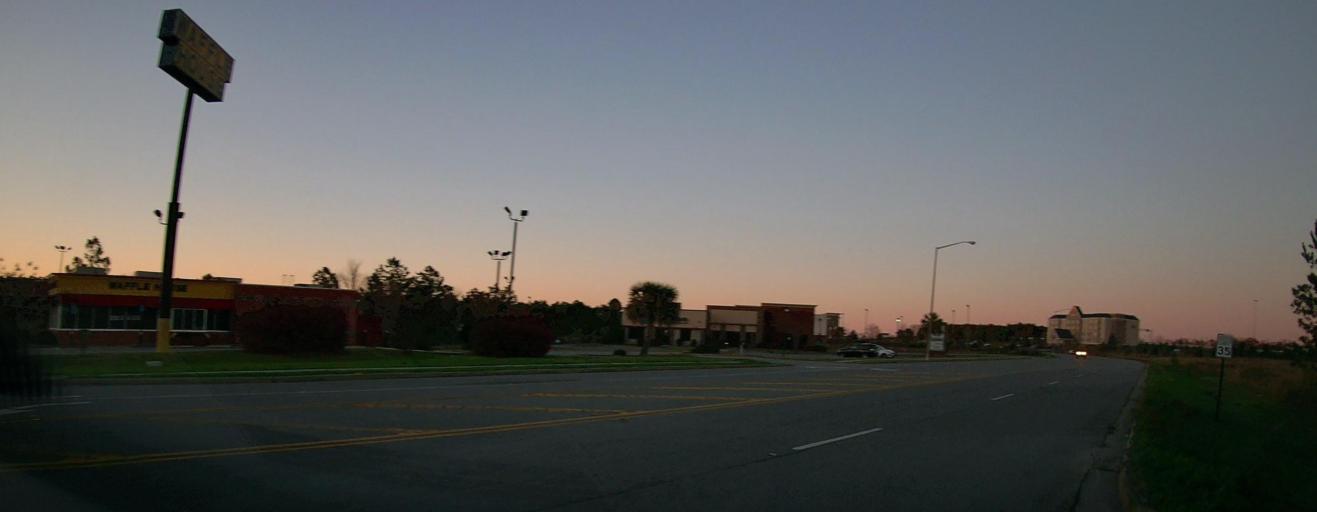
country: US
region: Georgia
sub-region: Crisp County
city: Cordele
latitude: 31.9345
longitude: -83.7510
